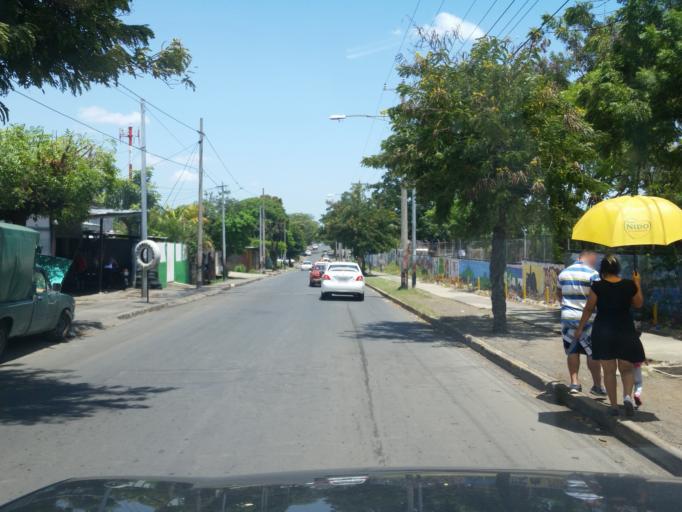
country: NI
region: Managua
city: Managua
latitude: 12.1238
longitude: -86.2141
